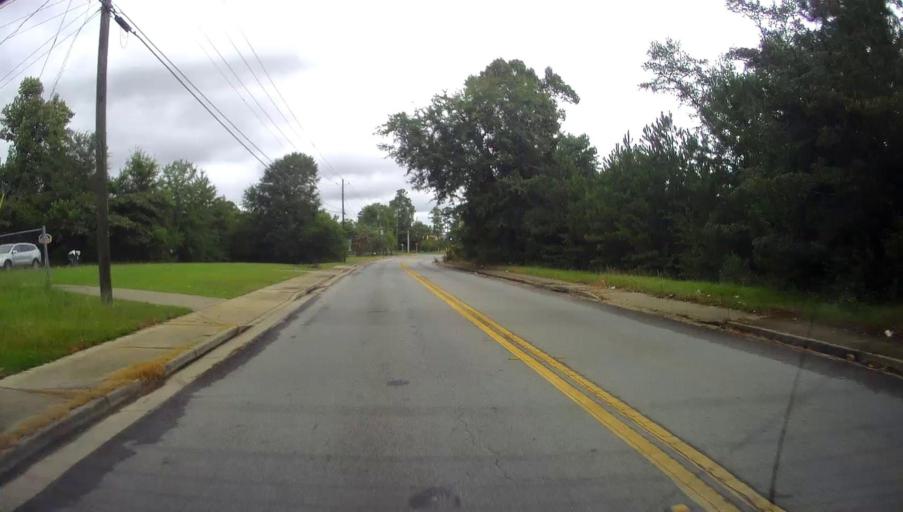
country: US
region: Georgia
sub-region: Bibb County
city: Macon
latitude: 32.8016
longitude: -83.7002
